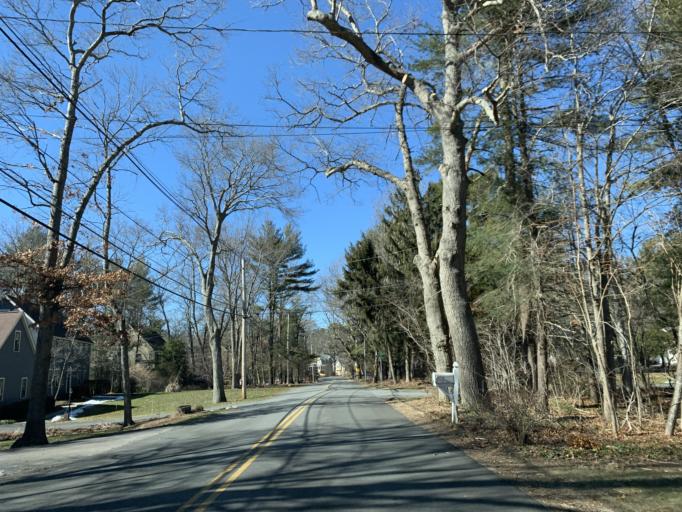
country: US
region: Massachusetts
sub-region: Bristol County
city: Norton
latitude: 41.9452
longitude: -71.1684
